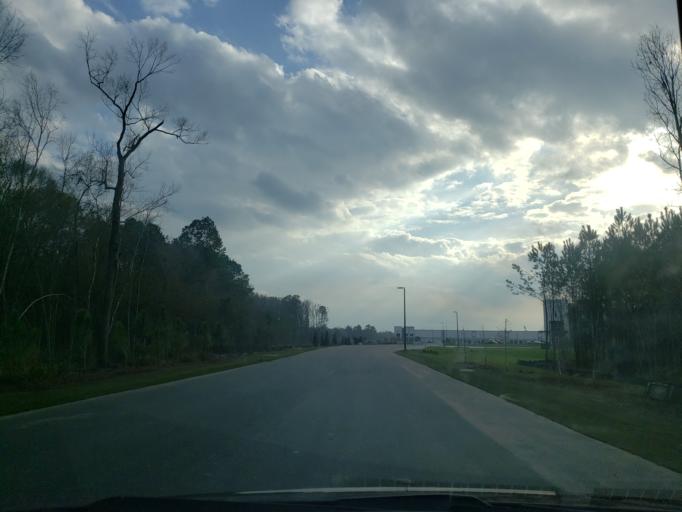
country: US
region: Georgia
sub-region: Effingham County
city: Rincon
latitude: 32.2350
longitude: -81.2068
